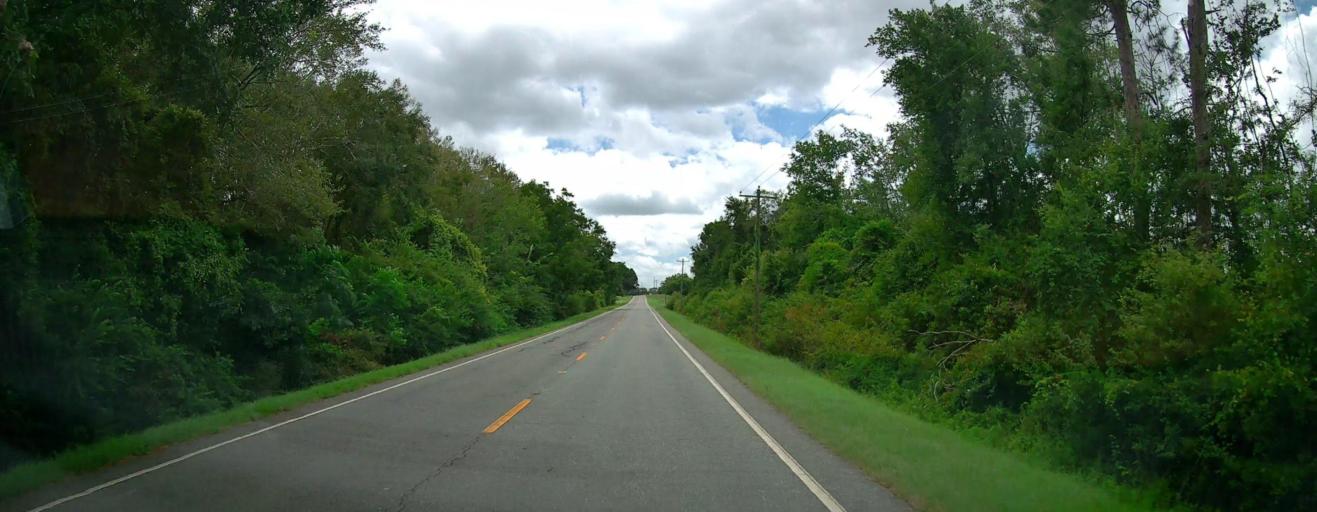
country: US
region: Georgia
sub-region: Wilcox County
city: Rochelle
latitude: 32.0044
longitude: -83.5578
